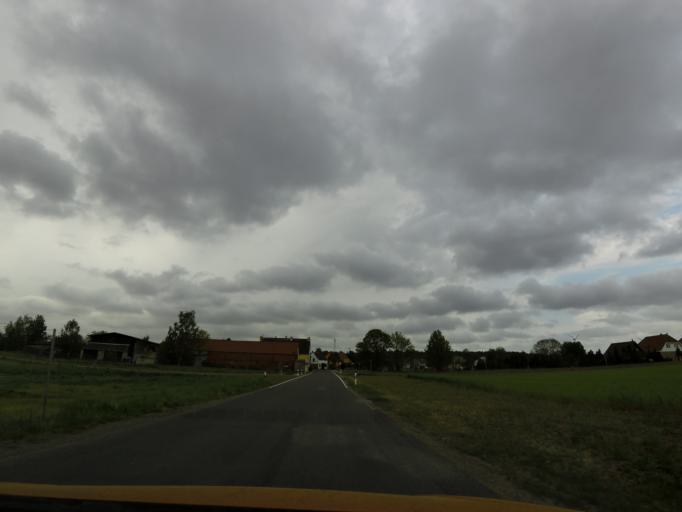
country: DE
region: Brandenburg
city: Linthe
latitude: 52.0923
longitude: 12.7578
